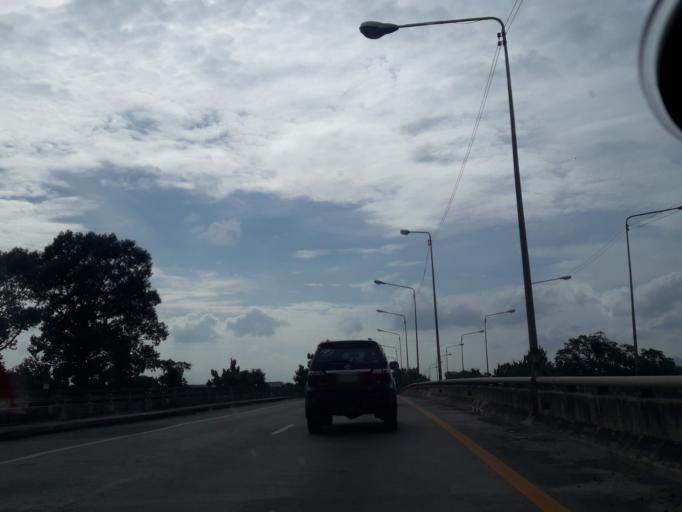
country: TH
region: Sara Buri
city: Saraburi
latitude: 14.5572
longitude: 100.9246
